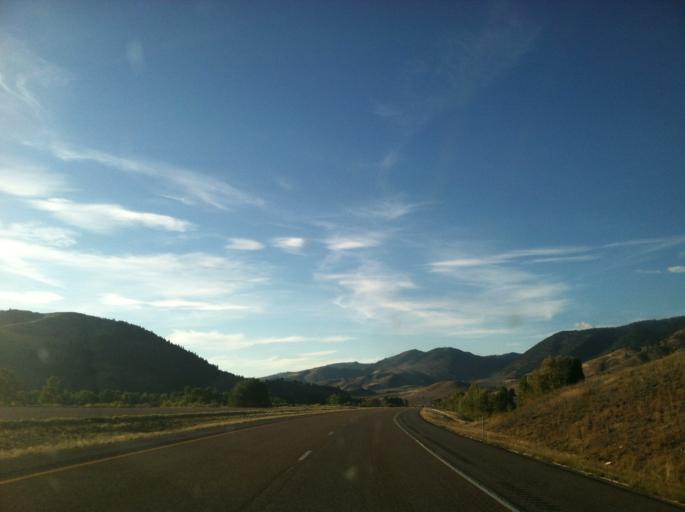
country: US
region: Montana
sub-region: Granite County
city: Philipsburg
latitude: 46.6835
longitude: -113.1930
